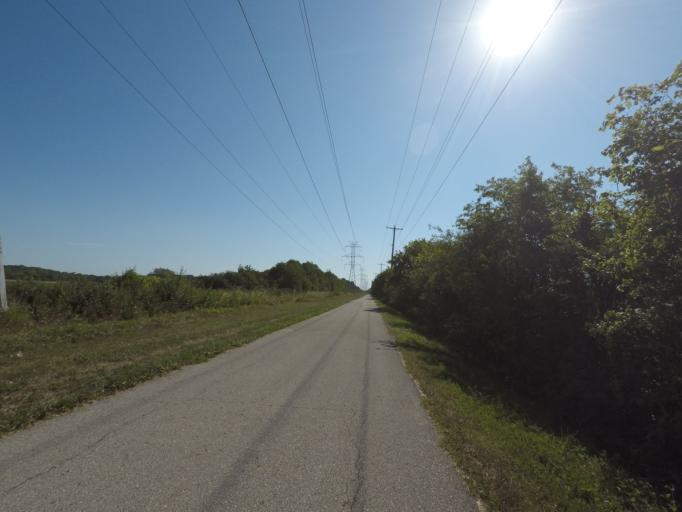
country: US
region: Wisconsin
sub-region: Waukesha County
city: New Berlin
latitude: 43.0100
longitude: -88.1450
